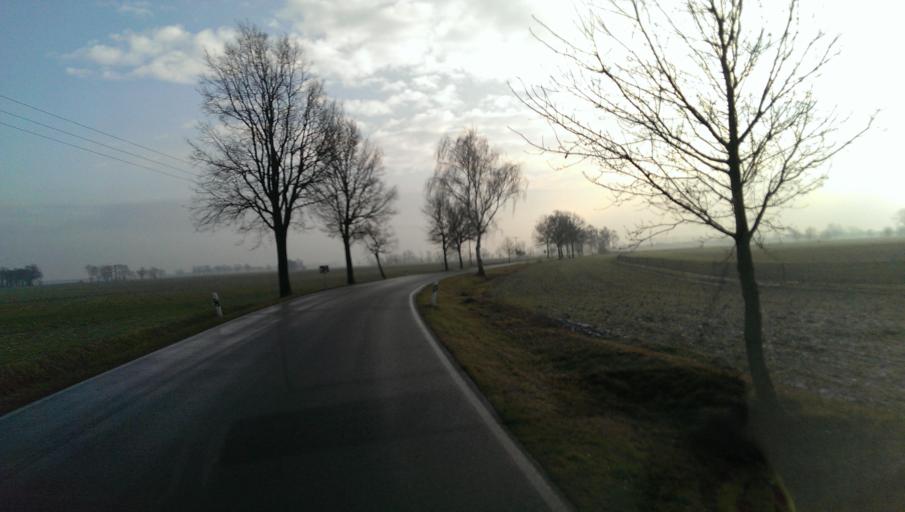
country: DE
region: Brandenburg
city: Bad Liebenwerda
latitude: 51.4731
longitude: 13.4244
